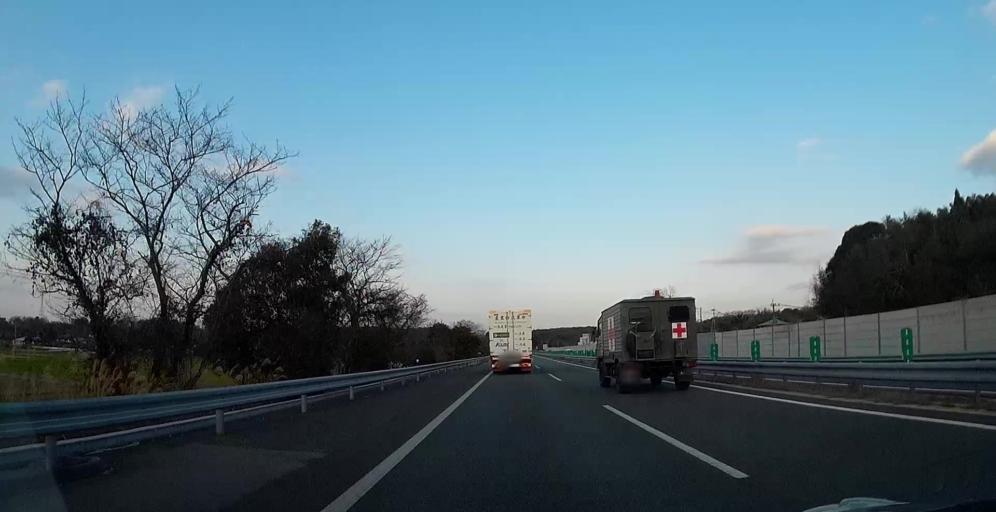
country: JP
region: Kumamoto
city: Kumamoto
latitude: 32.7399
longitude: 130.7816
